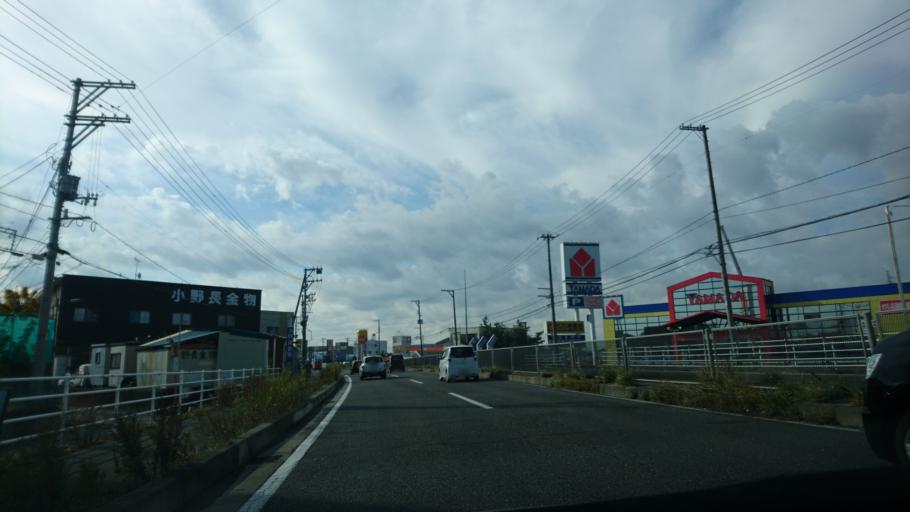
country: JP
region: Miyagi
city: Furukawa
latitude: 38.5810
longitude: 140.9460
